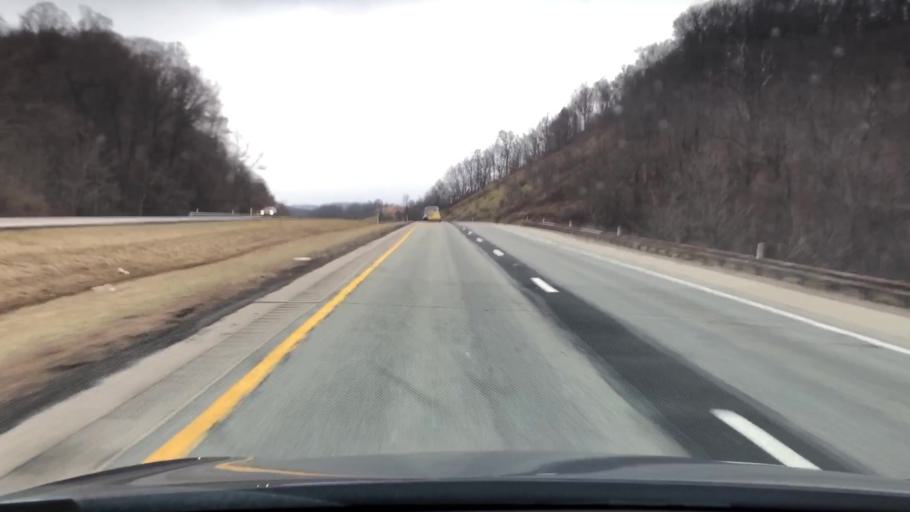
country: US
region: Pennsylvania
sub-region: Greene County
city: Morrisville
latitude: 39.8011
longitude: -80.0812
